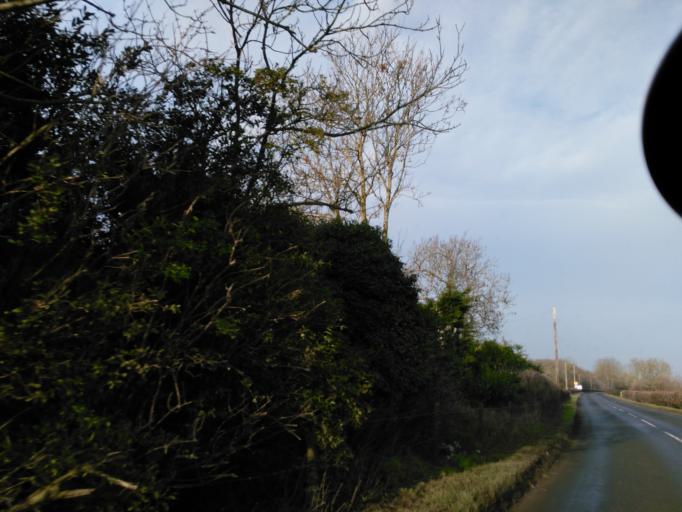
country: GB
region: England
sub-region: Wiltshire
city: Marston
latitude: 51.3224
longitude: -2.0556
